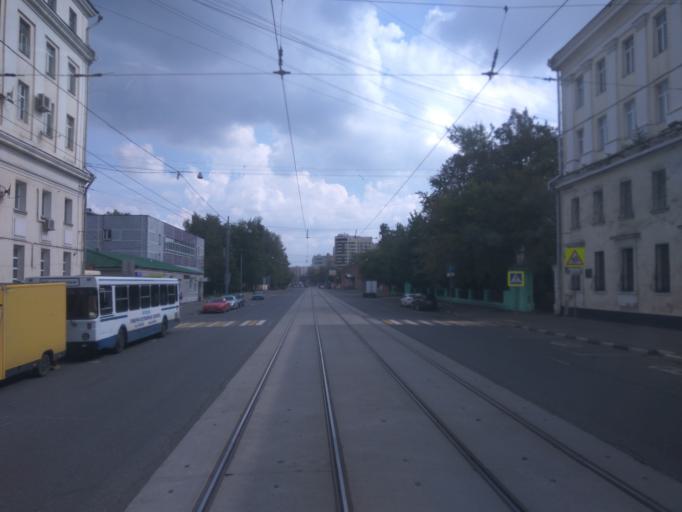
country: RU
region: Moscow
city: Lefortovo
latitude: 55.7606
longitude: 37.6897
